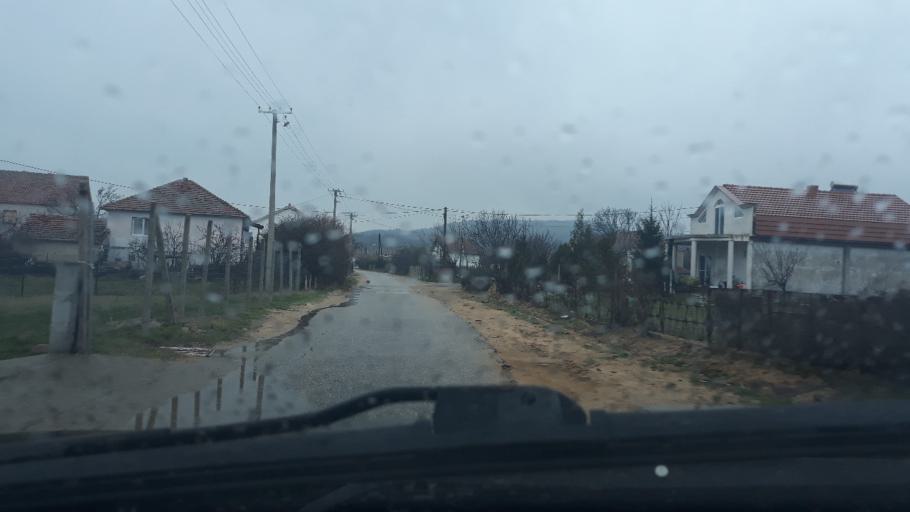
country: MK
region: Bogdanci
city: Bogdanci
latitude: 41.2453
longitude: 22.6120
